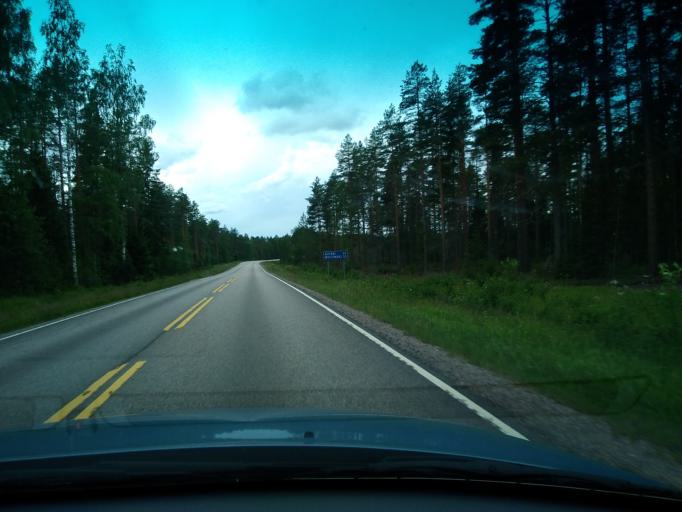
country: FI
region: Central Finland
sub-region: Saarijaervi-Viitasaari
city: Pylkoenmaeki
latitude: 62.6236
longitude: 24.7805
